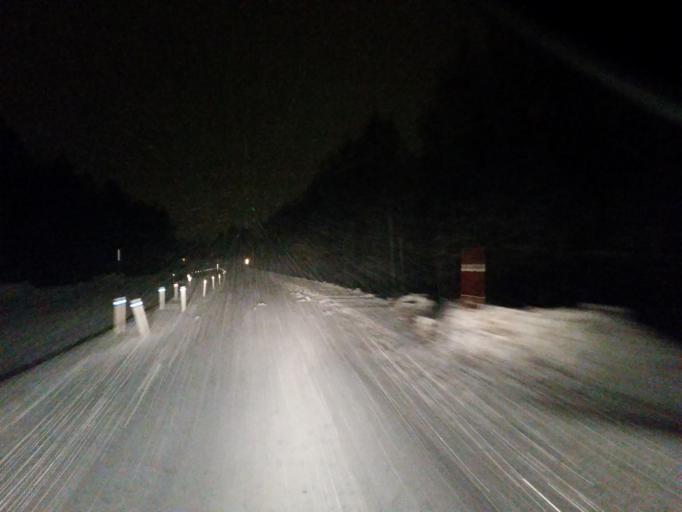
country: SE
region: Norrbotten
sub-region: Pitea Kommun
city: Pitea
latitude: 65.2983
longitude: 21.5104
